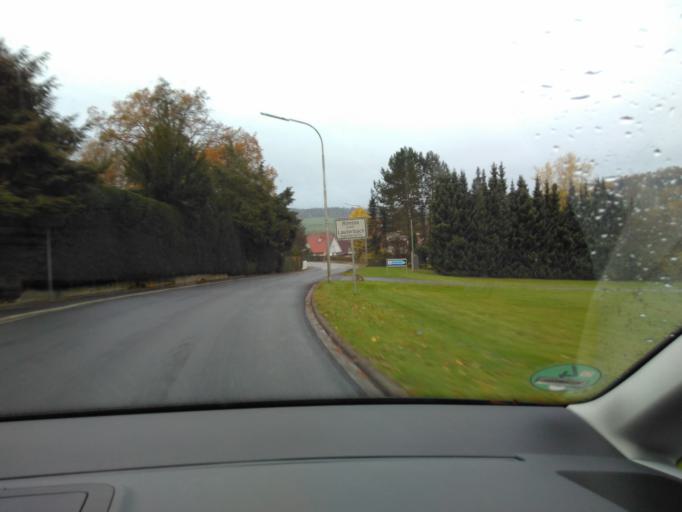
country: DE
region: Hesse
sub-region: Regierungsbezirk Giessen
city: Lauterbach
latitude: 50.6439
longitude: 9.3814
